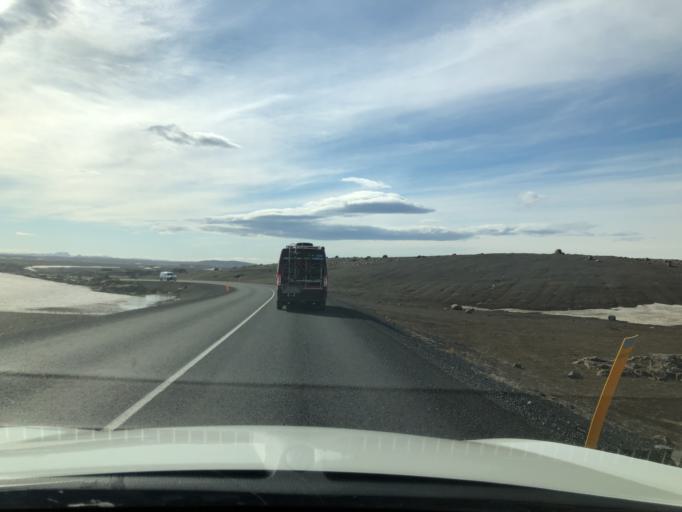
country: IS
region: Northeast
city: Husavik
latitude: 65.8114
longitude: -16.4062
